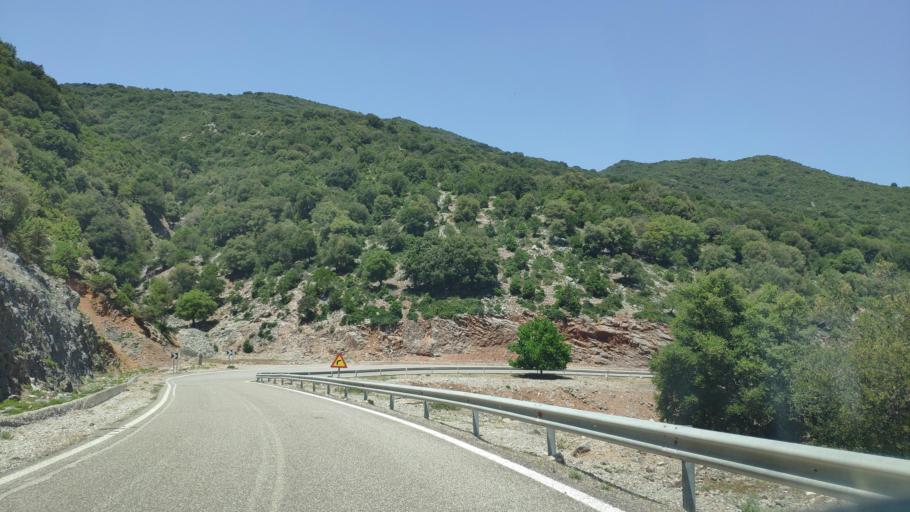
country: GR
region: Central Greece
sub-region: Nomos Evrytanias
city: Kerasochori
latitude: 39.0897
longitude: 21.4120
